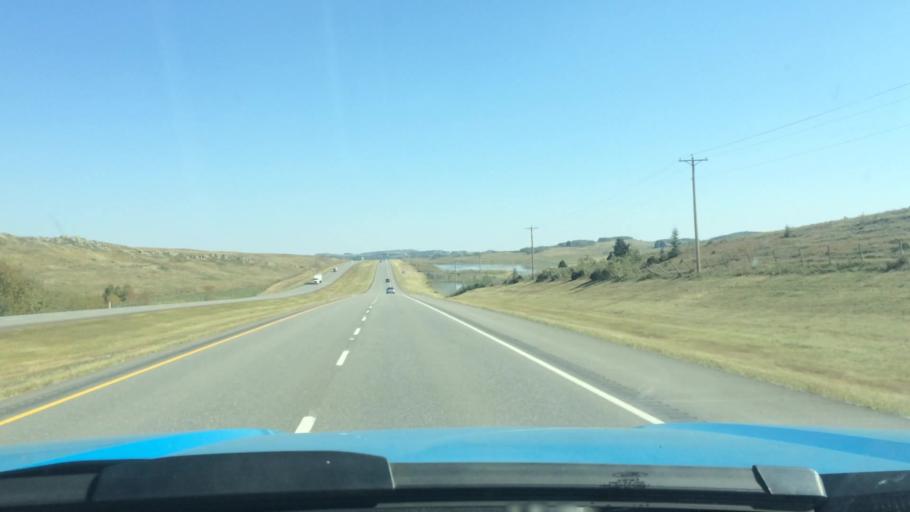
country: CA
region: Alberta
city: Cochrane
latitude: 51.1199
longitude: -114.6665
